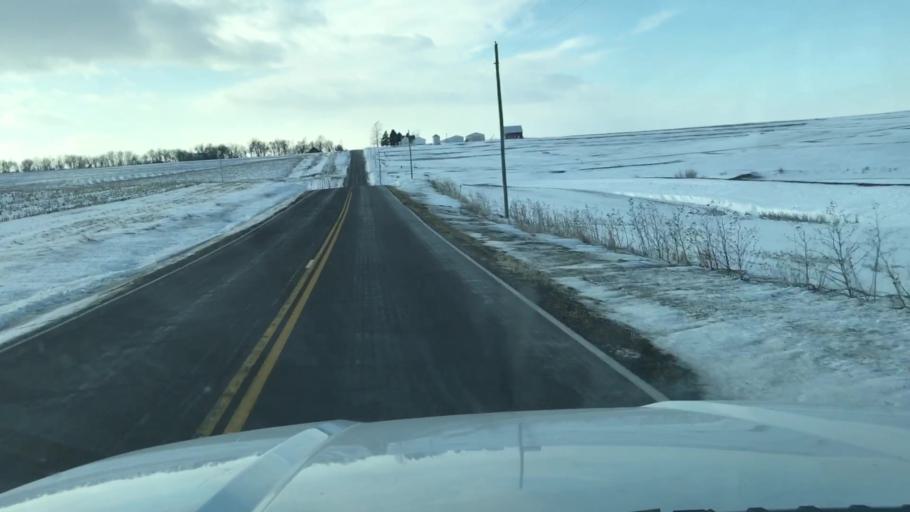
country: US
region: Missouri
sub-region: Nodaway County
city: Maryville
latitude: 40.2012
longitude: -94.9117
